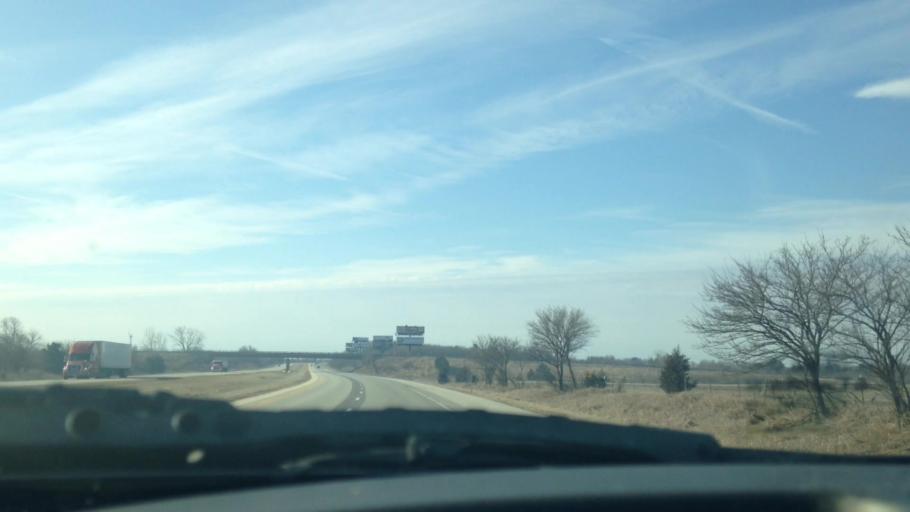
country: US
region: Illinois
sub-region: Ford County
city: Paxton
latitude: 40.5206
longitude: -88.0847
